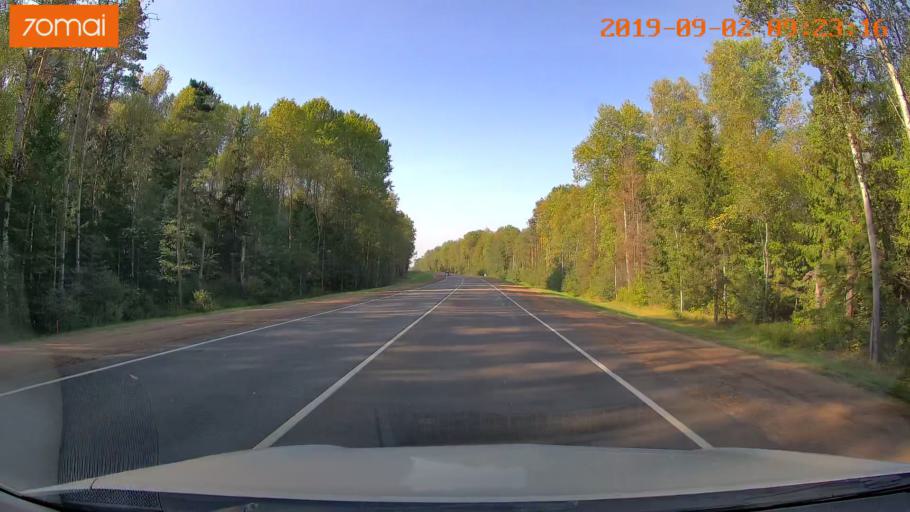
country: RU
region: Kaluga
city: Yukhnov
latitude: 54.7776
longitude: 35.3187
